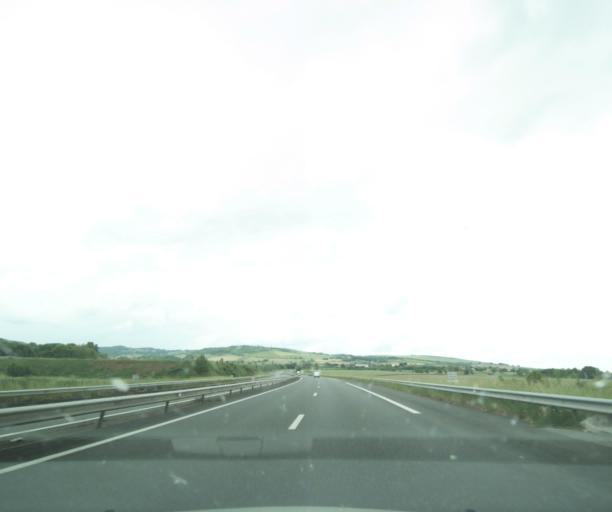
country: FR
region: Auvergne
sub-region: Departement du Puy-de-Dome
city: Saint-Bonnet-pres-Riom
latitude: 45.9495
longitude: 3.1167
